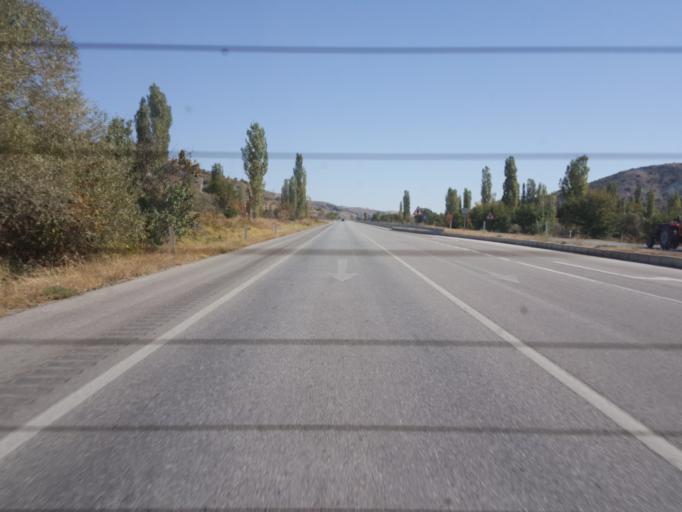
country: TR
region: Corum
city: Sungurlu
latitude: 40.1902
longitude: 34.5005
